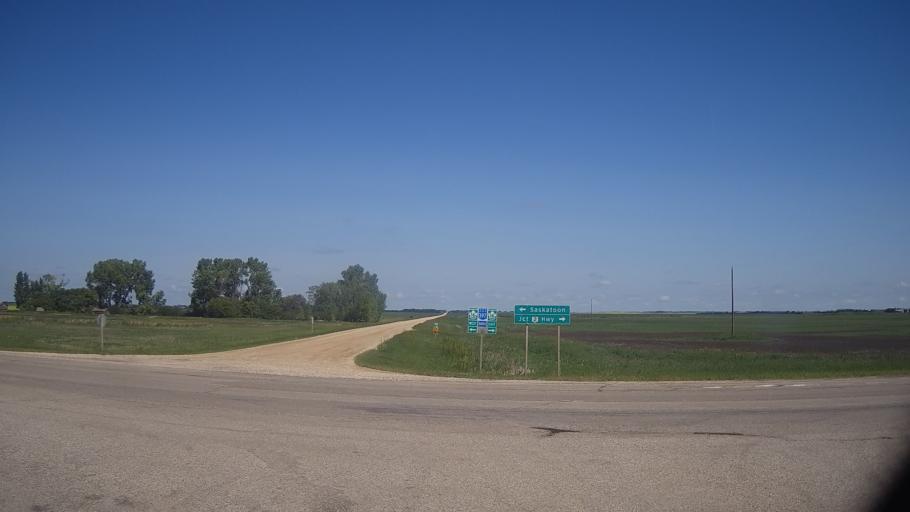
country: CA
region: Saskatchewan
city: Saskatoon
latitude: 51.9911
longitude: -106.0755
